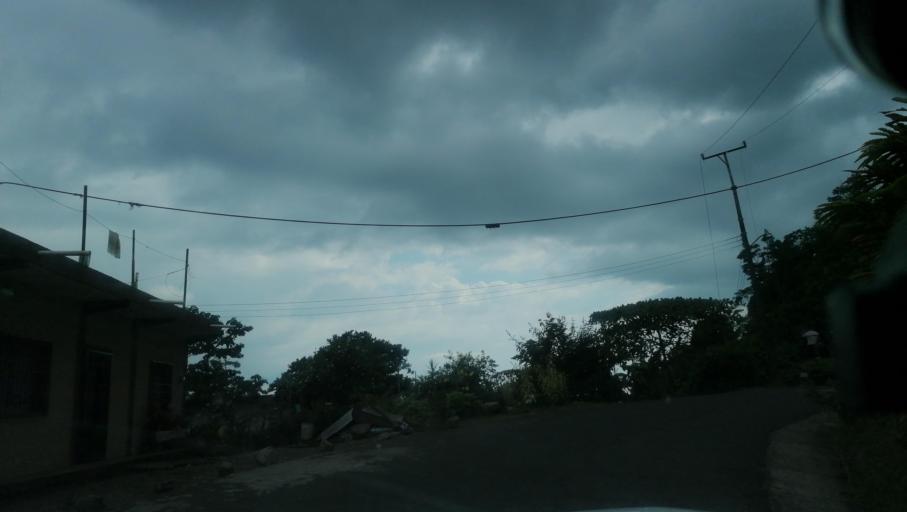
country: MX
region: Chiapas
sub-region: Cacahoatan
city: Benito Juarez
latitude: 15.0732
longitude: -92.1736
